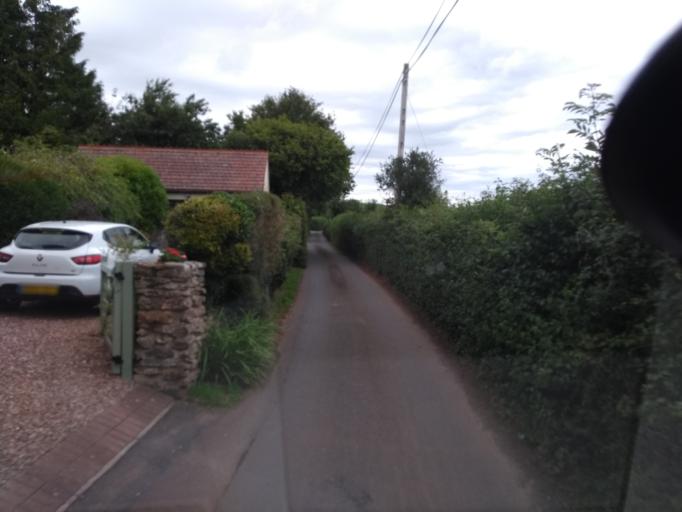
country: GB
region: England
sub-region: Somerset
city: North Petherton
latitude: 51.1312
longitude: -3.0926
